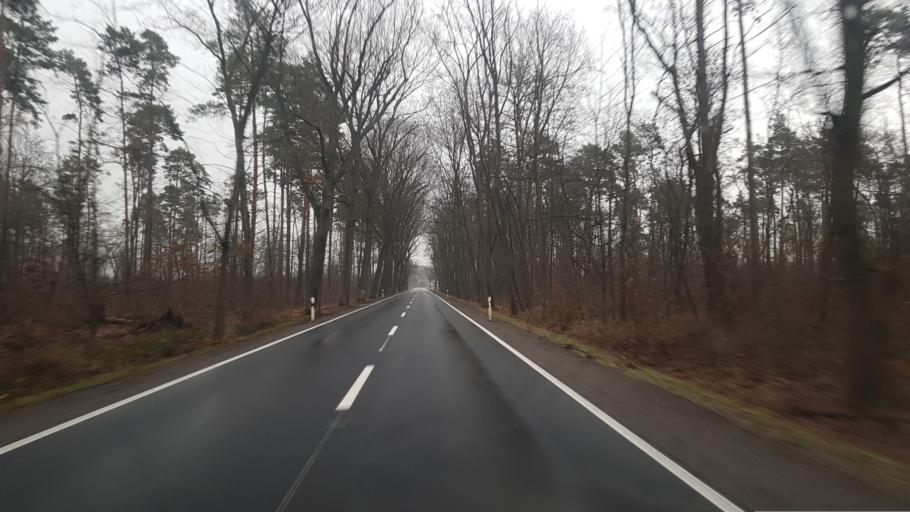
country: DE
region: Brandenburg
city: Altdobern
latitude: 51.7149
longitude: 14.0285
